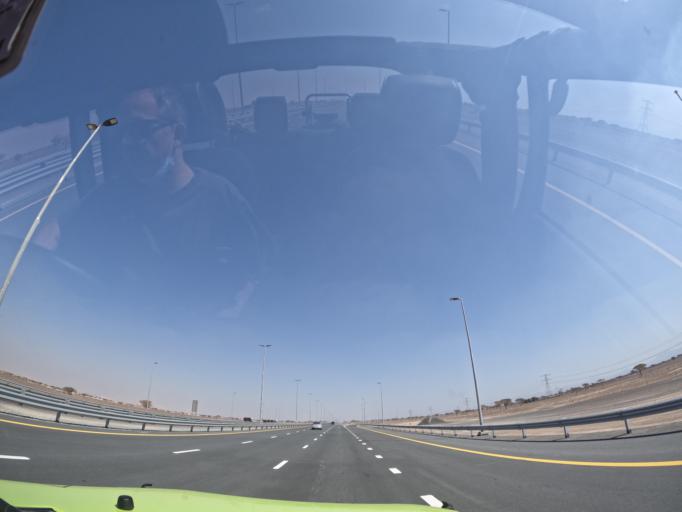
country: AE
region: Ash Shariqah
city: Adh Dhayd
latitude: 24.9520
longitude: 55.8354
